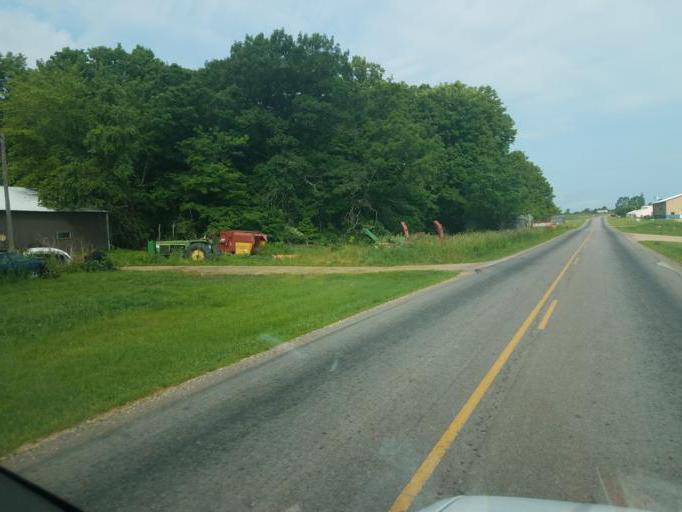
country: US
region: Wisconsin
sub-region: Vernon County
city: Hillsboro
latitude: 43.6121
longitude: -90.4405
